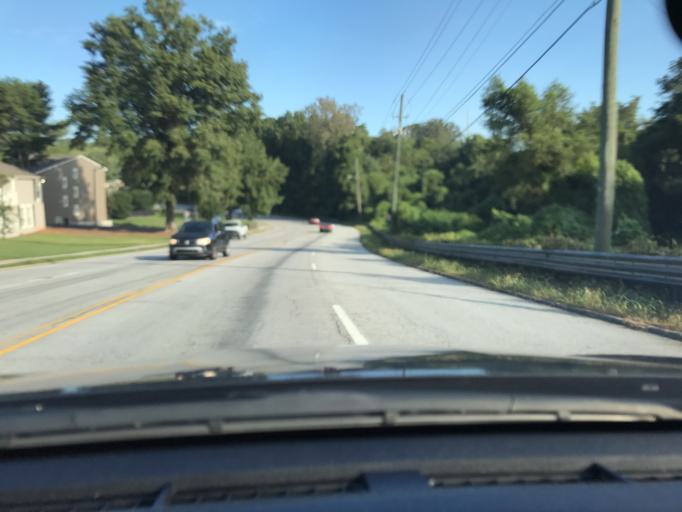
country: US
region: Georgia
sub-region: DeKalb County
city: Scottdale
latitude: 33.7799
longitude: -84.2447
